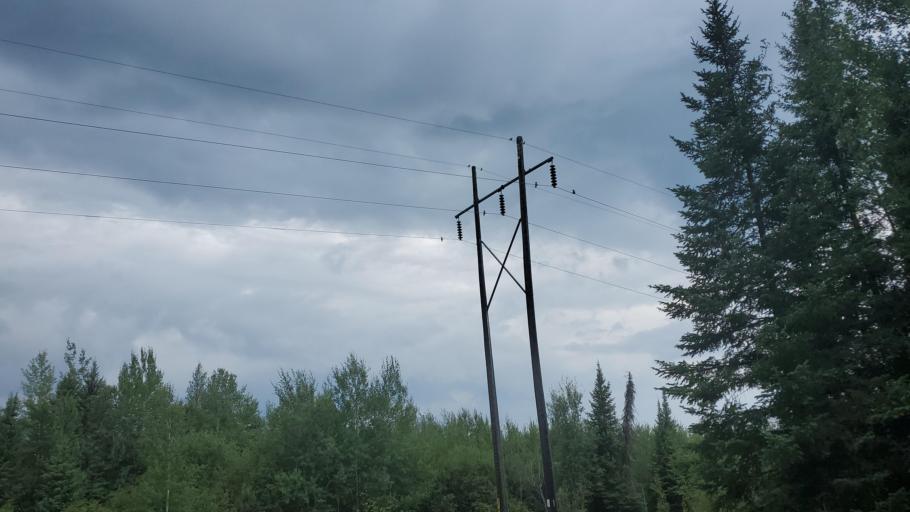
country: CA
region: Ontario
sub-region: Rainy River District
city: Atikokan
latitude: 49.5978
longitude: -91.3843
